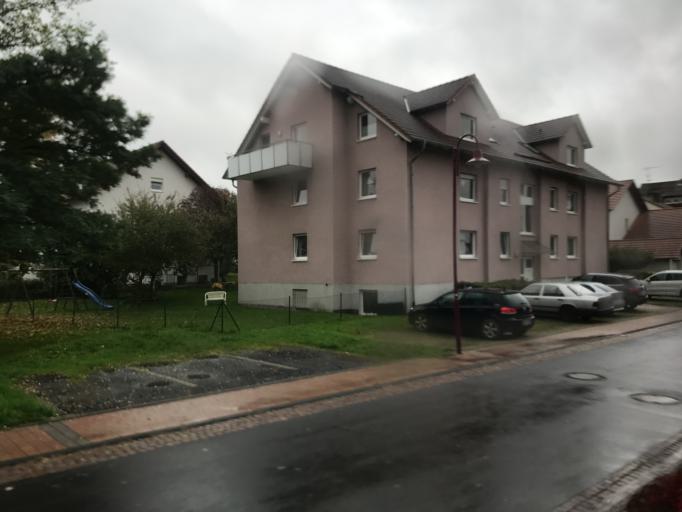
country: DE
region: Hesse
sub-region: Regierungsbezirk Kassel
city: Kaufungen
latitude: 51.2838
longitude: 9.6107
